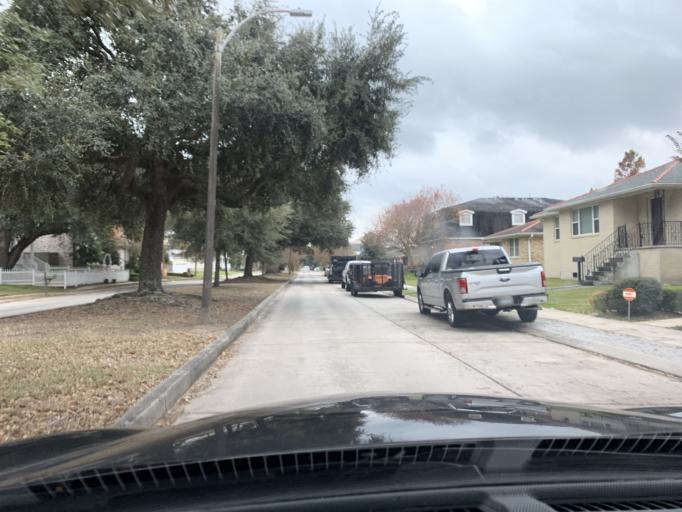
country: US
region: Louisiana
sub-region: Jefferson Parish
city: Metairie
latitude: 30.0148
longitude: -90.1016
